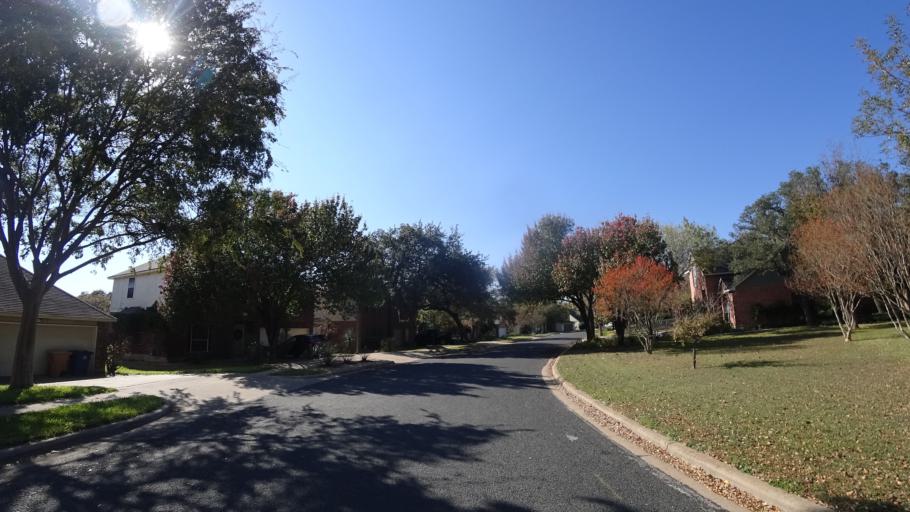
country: US
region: Texas
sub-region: Travis County
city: Shady Hollow
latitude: 30.2197
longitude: -97.8626
